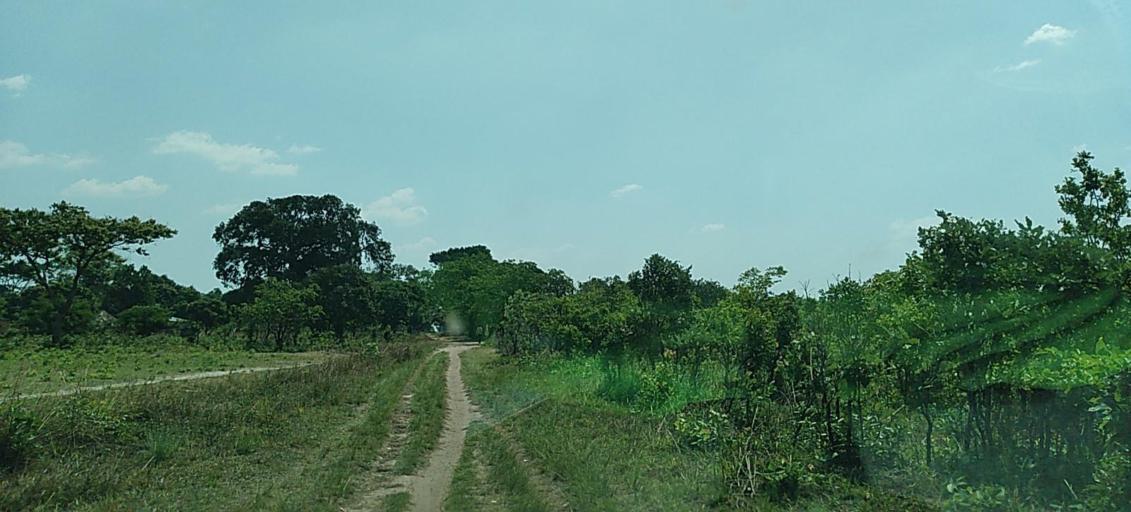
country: CD
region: Katanga
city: Kolwezi
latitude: -11.2807
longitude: 25.1523
